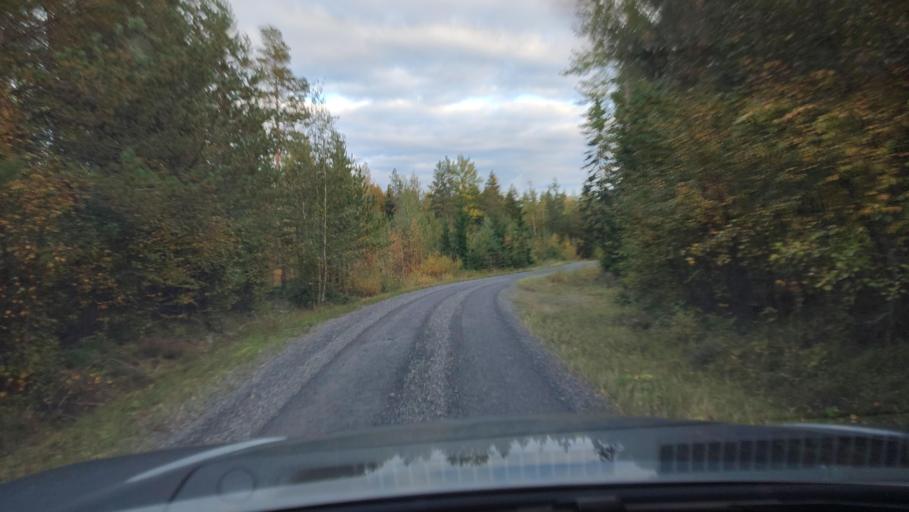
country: FI
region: Ostrobothnia
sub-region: Sydosterbotten
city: Kristinestad
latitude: 62.2315
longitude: 21.4170
